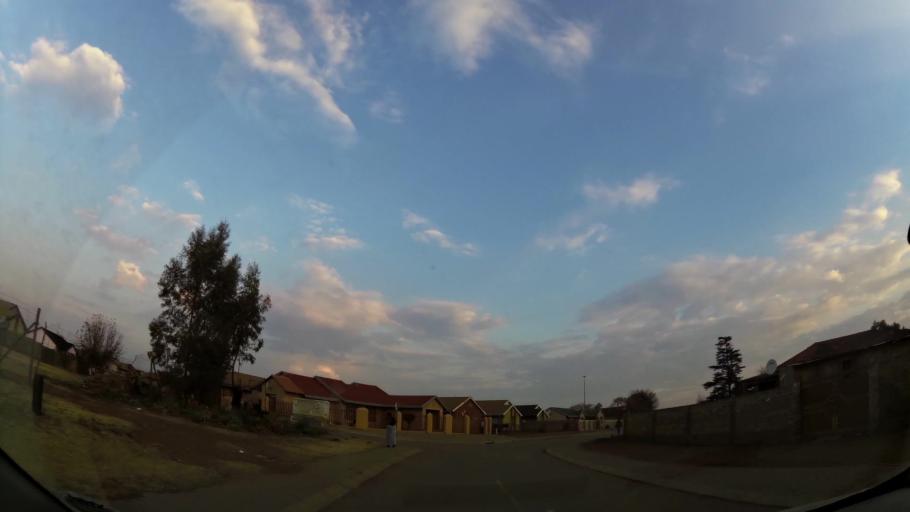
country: ZA
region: Gauteng
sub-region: City of Johannesburg Metropolitan Municipality
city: Orange Farm
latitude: -26.5436
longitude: 27.8853
